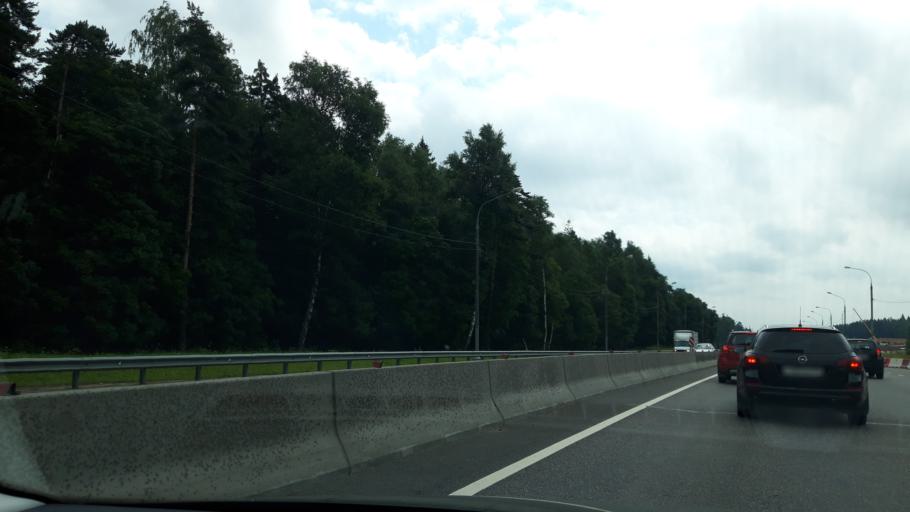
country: RU
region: Moskovskaya
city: Lozhki
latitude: 56.0872
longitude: 37.1155
